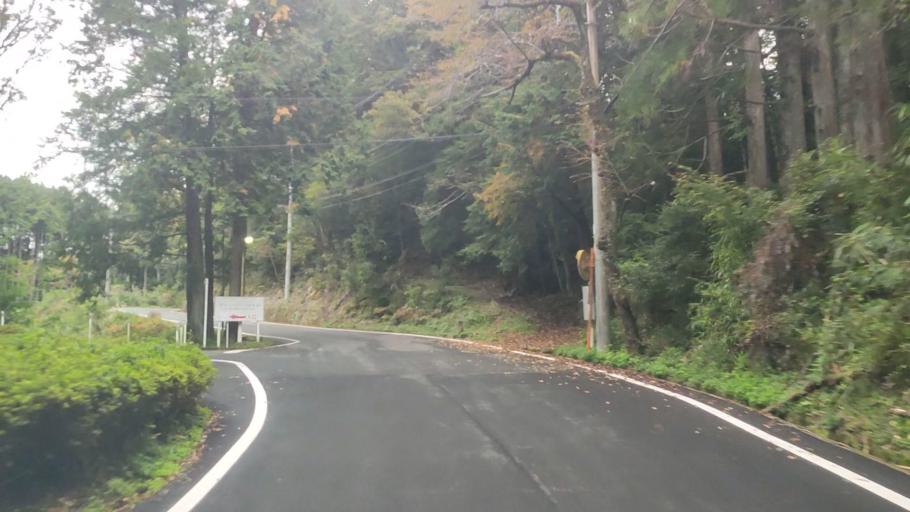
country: JP
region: Shizuoka
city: Ito
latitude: 34.9144
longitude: 138.9861
